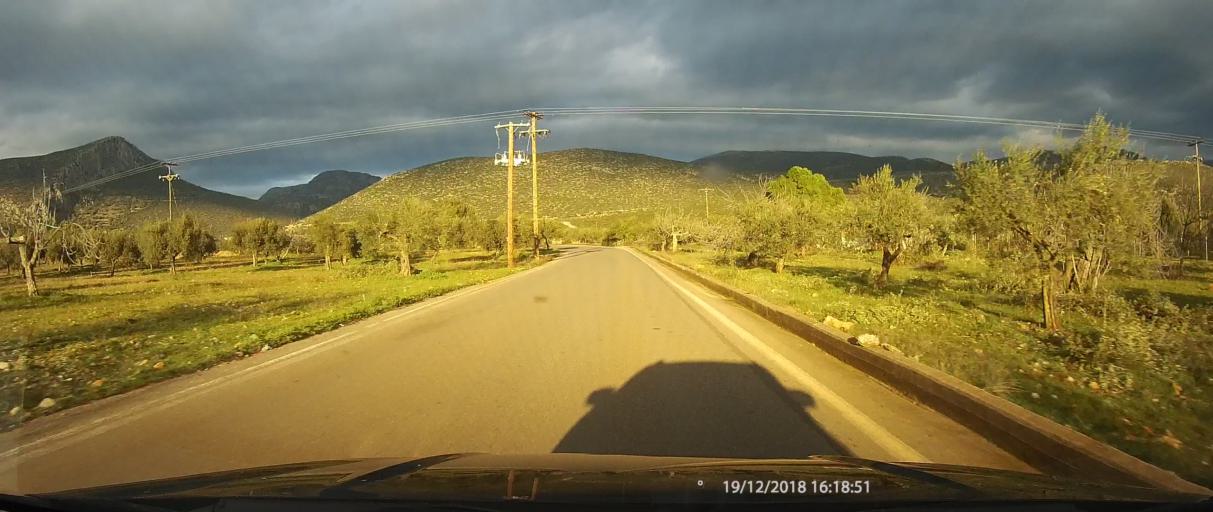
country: GR
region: Peloponnese
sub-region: Nomos Lakonias
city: Kato Glikovrisi
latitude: 36.9273
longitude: 22.8211
